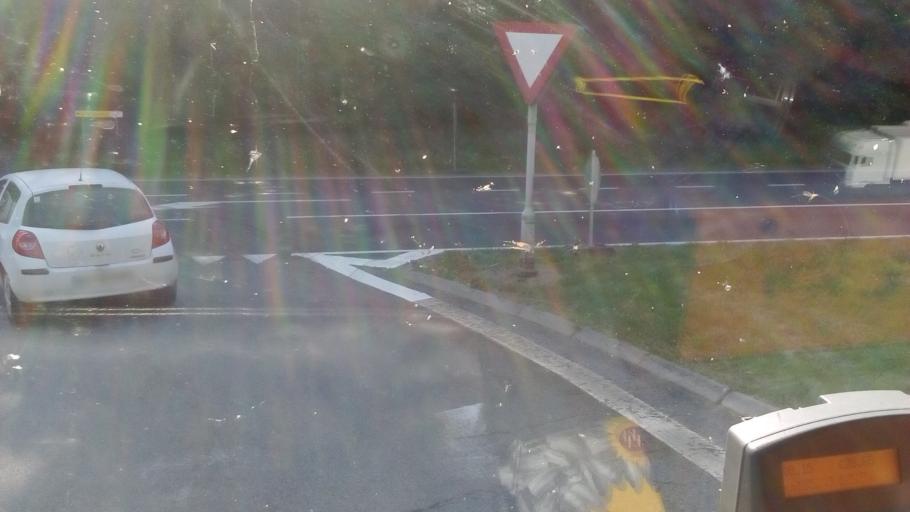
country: BE
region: Wallonia
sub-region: Province du Luxembourg
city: Aubange
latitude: 49.5556
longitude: 5.8082
